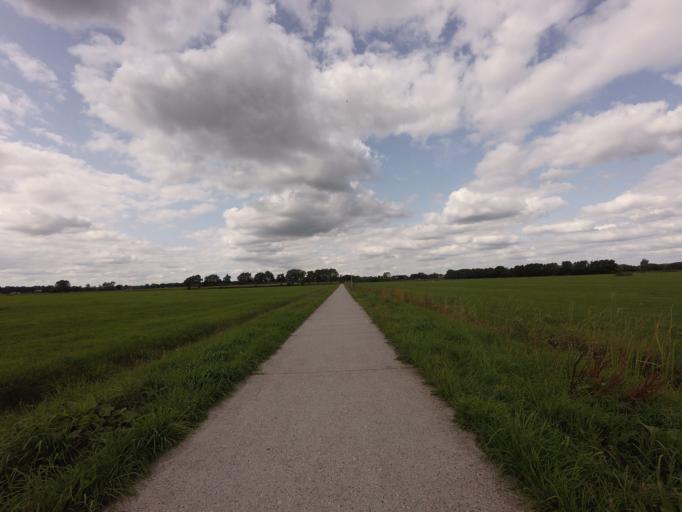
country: NL
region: Drenthe
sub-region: Gemeente De Wolden
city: Ruinen
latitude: 52.7516
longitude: 6.3649
